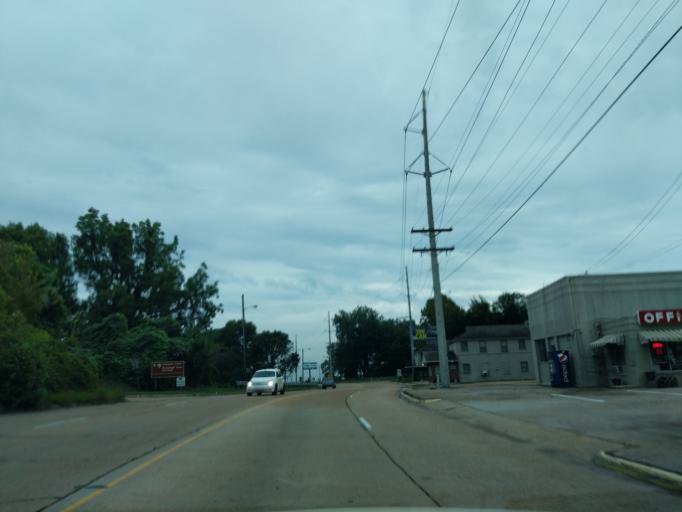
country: US
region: Mississippi
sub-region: Warren County
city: Vicksburg
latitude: 32.3196
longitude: -90.8967
